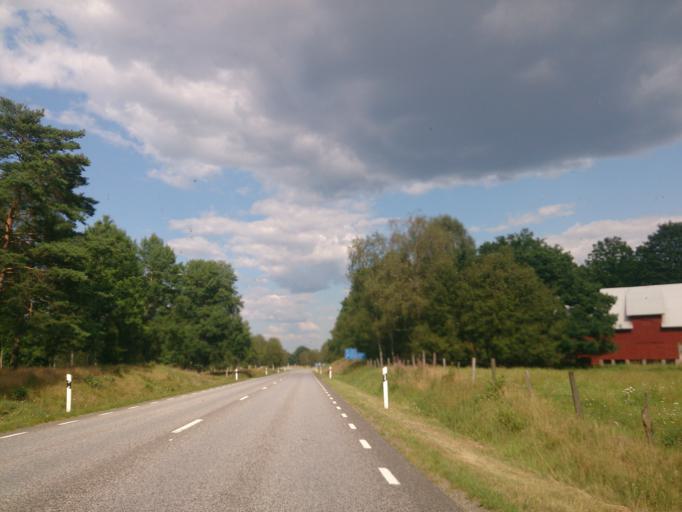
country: SE
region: Joenkoeping
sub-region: Gislaveds Kommun
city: Reftele
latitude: 57.1610
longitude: 13.5535
